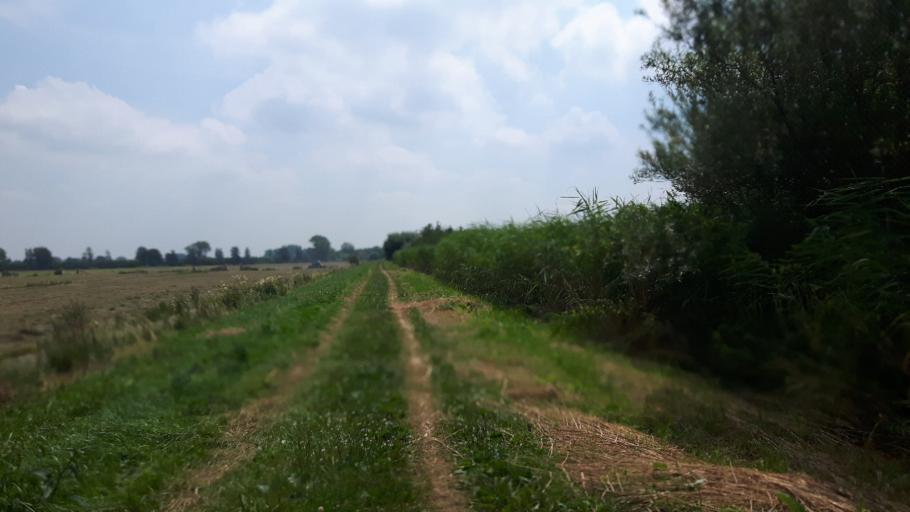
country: NL
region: Utrecht
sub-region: Gemeente Lopik
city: Lopik
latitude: 51.9489
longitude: 4.9922
